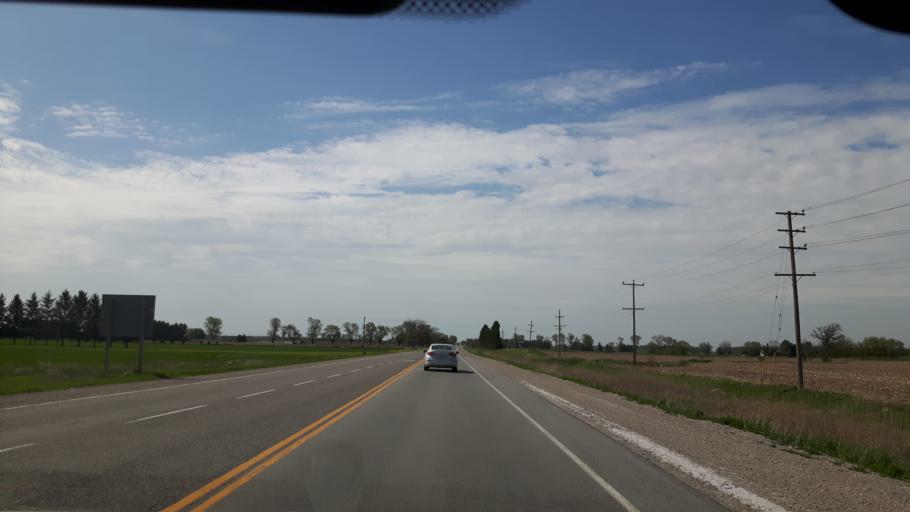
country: CA
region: Ontario
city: South Huron
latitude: 43.2701
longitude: -81.4652
